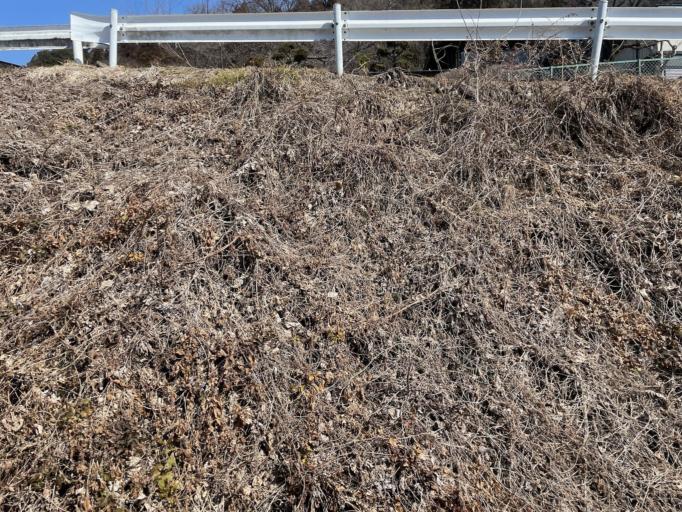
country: JP
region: Gunma
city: Nakanojomachi
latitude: 36.5612
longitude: 138.7664
